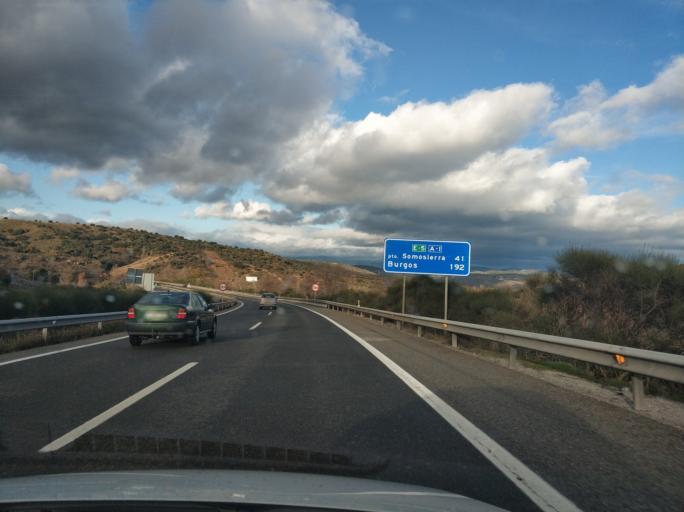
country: ES
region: Madrid
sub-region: Provincia de Madrid
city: Venturada
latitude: 40.7970
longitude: -3.6164
